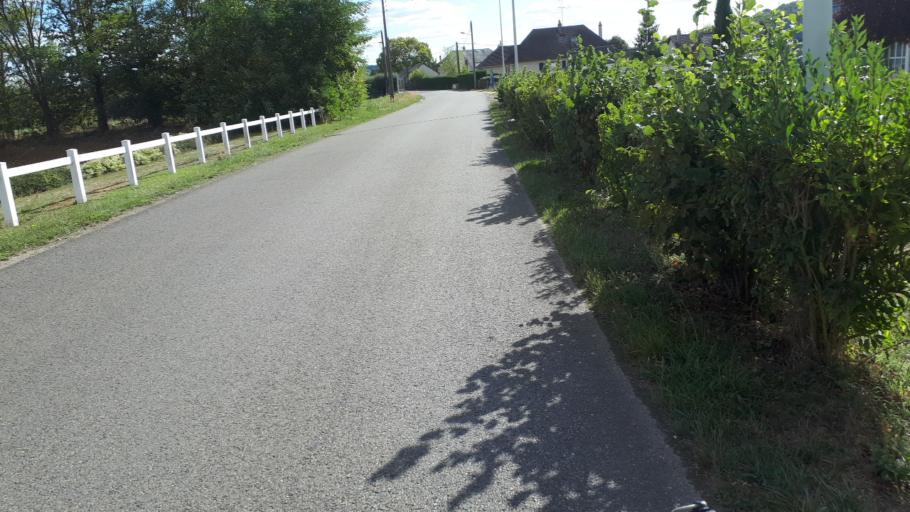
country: FR
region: Centre
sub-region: Departement du Loir-et-Cher
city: Villiers-sur-Loir
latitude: 47.7942
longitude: 0.9616
